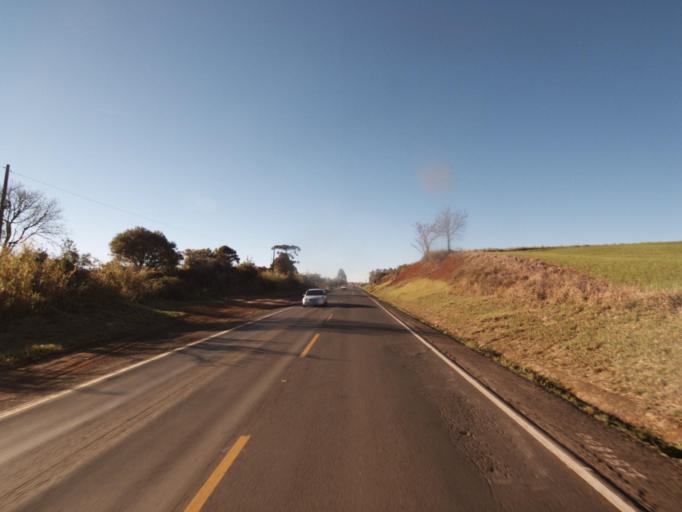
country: AR
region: Misiones
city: Bernardo de Irigoyen
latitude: -26.3173
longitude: -53.5495
